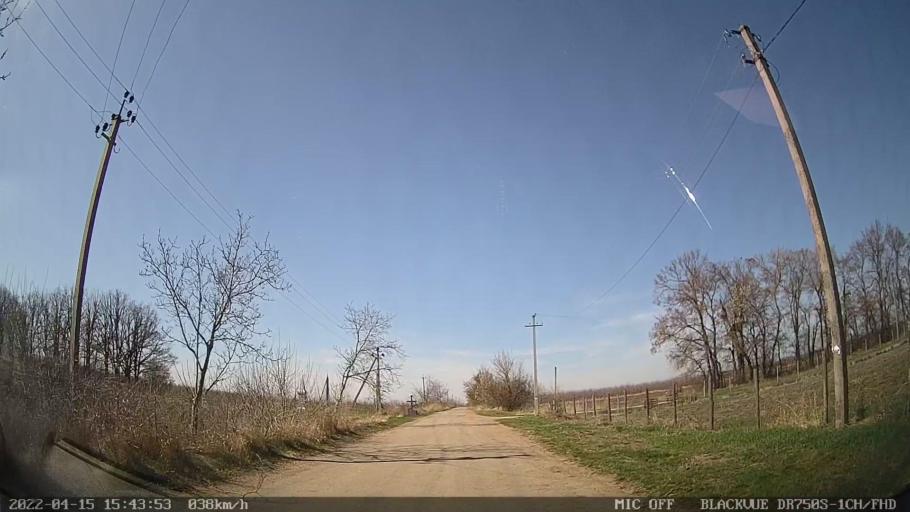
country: MD
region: Raionul Ocnita
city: Otaci
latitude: 48.3673
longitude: 27.9247
